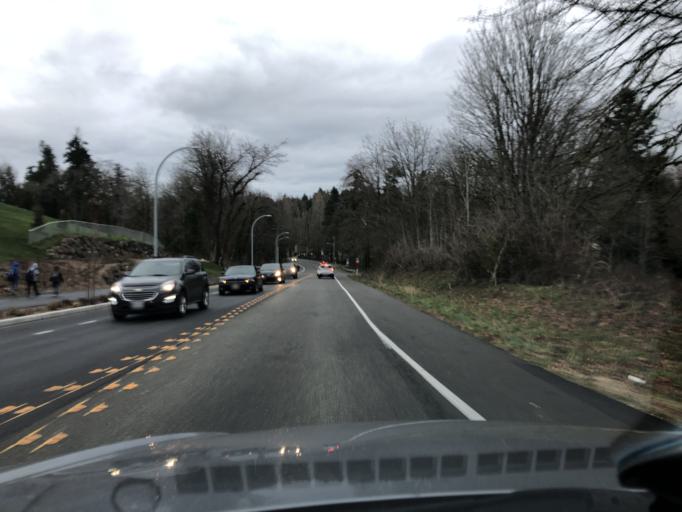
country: US
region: Washington
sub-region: King County
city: Des Moines
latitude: 47.3883
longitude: -122.3126
